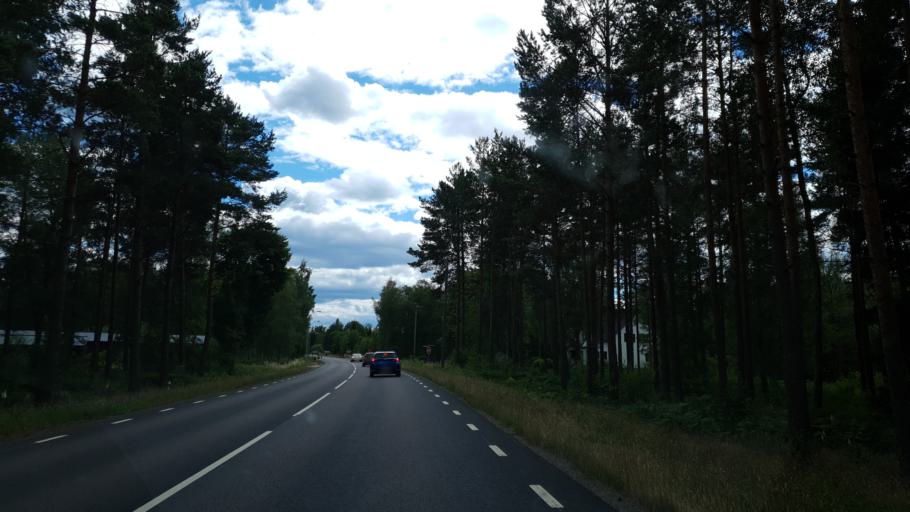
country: SE
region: Kalmar
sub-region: Emmaboda Kommun
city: Emmaboda
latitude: 56.9230
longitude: 15.5714
